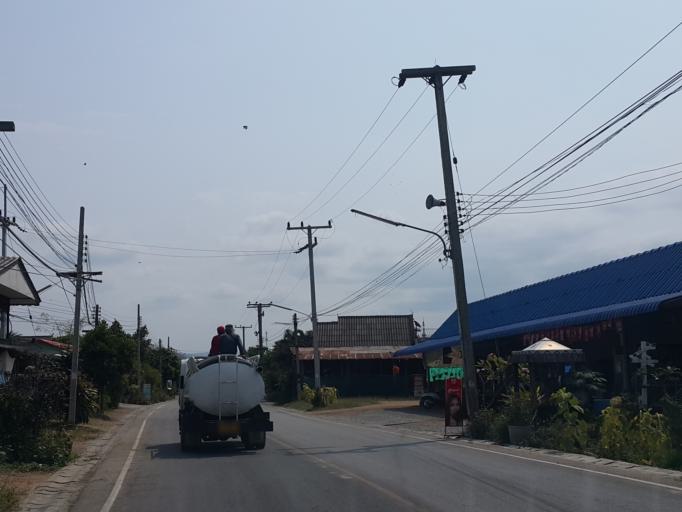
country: TH
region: Lamphun
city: Ban Thi
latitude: 18.6545
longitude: 99.1187
